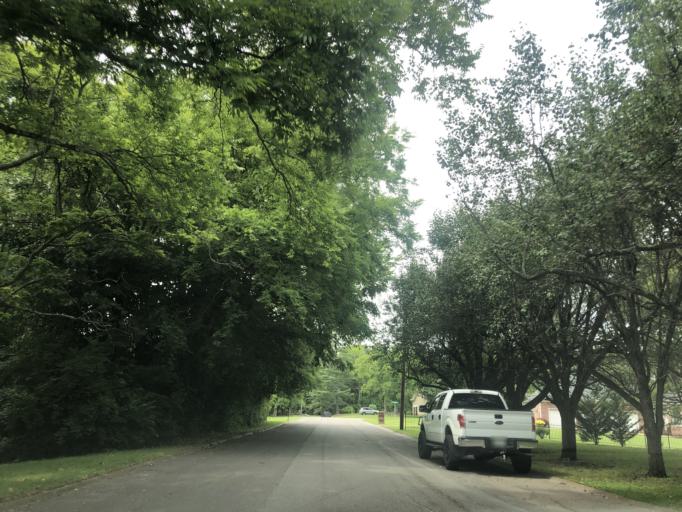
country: US
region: Tennessee
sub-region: Davidson County
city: Nashville
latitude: 36.2106
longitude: -86.8065
